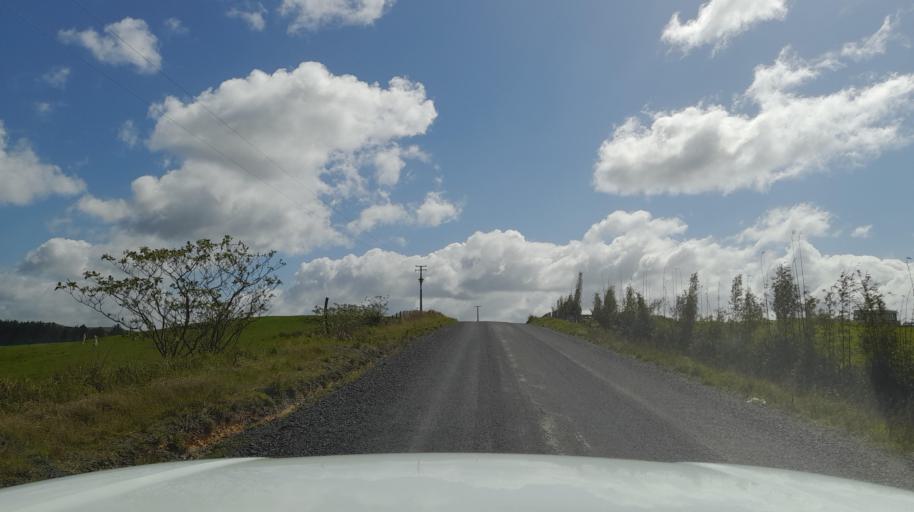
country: NZ
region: Northland
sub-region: Far North District
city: Kerikeri
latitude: -35.2217
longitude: 173.8715
